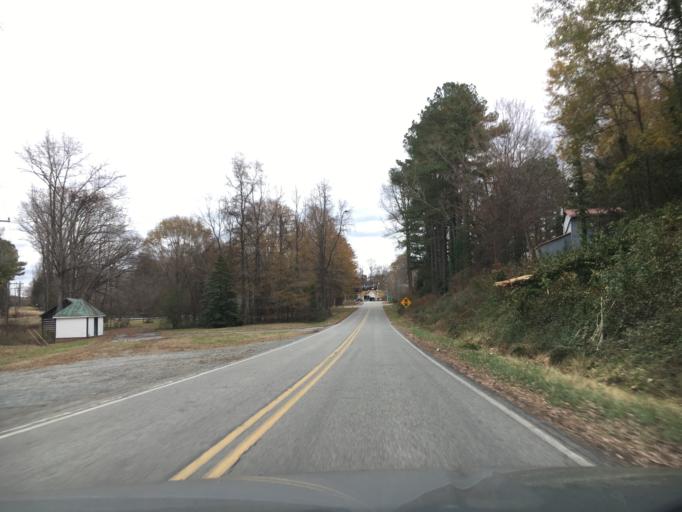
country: US
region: Virginia
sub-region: Halifax County
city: South Boston
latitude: 36.7049
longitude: -78.8919
